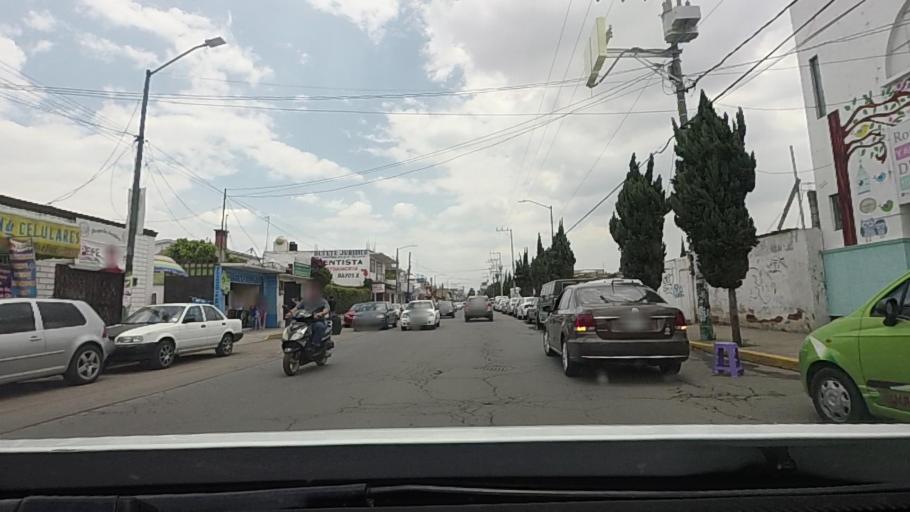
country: MX
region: Mexico
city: Chalco de Diaz Covarrubias
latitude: 19.2591
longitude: -98.8928
